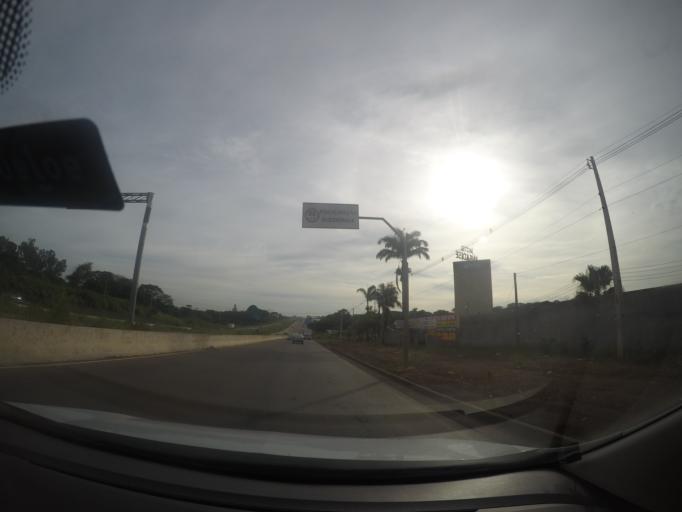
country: BR
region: Goias
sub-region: Goiania
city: Goiania
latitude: -16.7114
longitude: -49.3550
